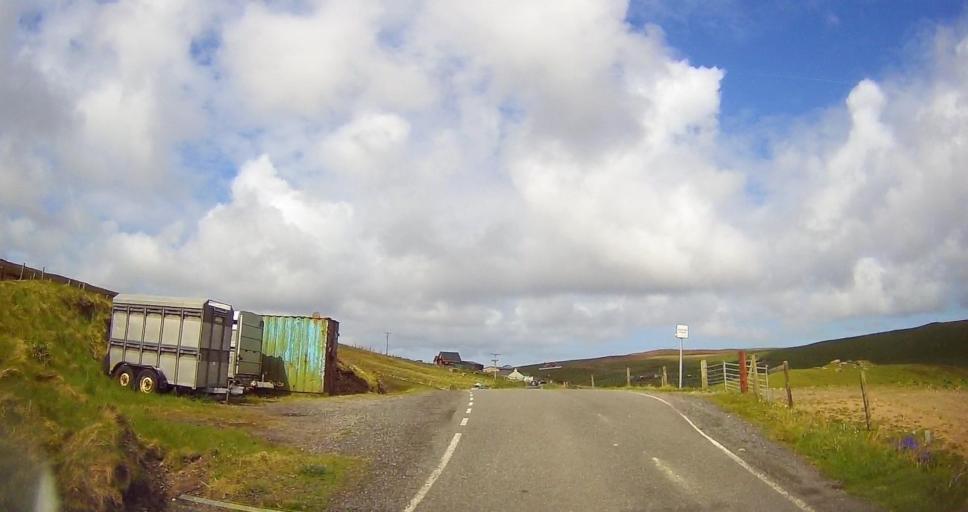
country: GB
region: Scotland
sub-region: Shetland Islands
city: Lerwick
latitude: 60.3010
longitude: -1.3430
